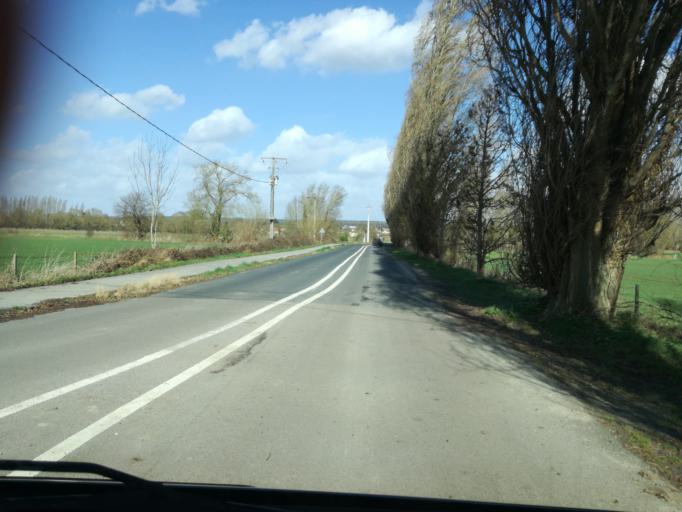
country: FR
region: Haute-Normandie
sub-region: Departement de la Seine-Maritime
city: Sahurs
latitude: 49.3539
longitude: 0.9352
